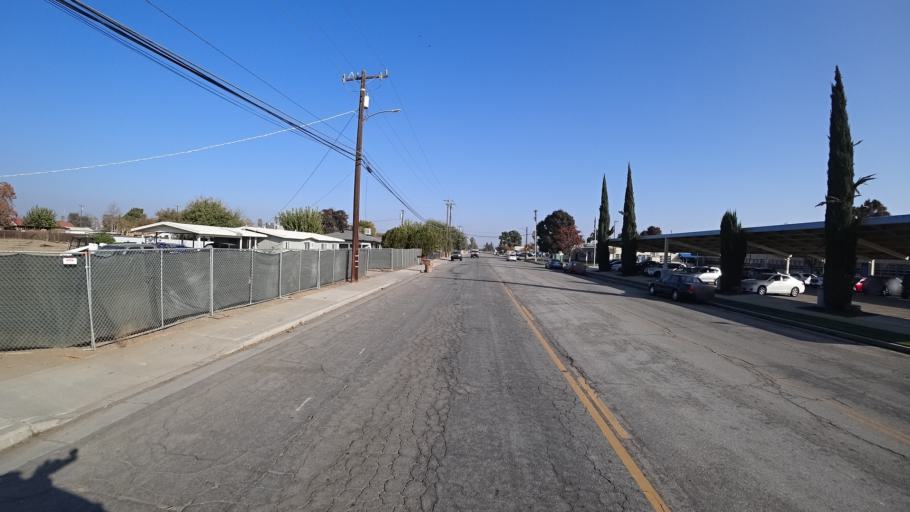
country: US
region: California
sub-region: Kern County
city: Greenfield
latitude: 35.2741
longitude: -119.0062
